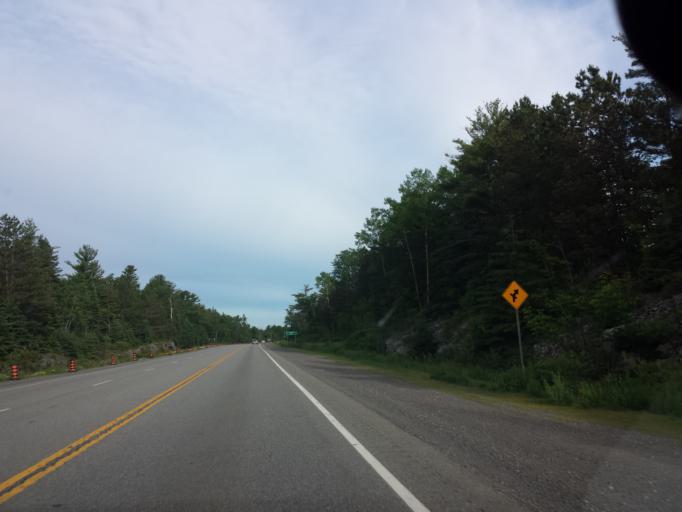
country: CA
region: Ontario
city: Arnprior
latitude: 45.4372
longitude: -76.4480
